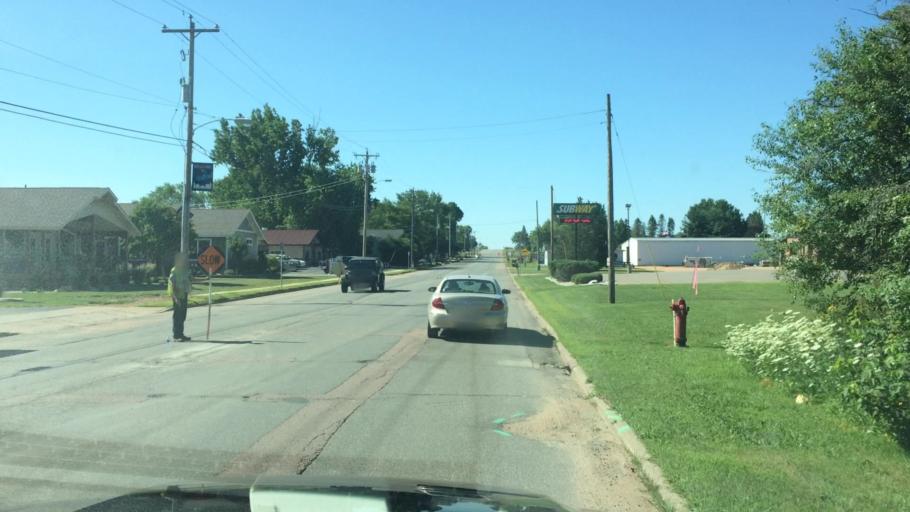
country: US
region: Wisconsin
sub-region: Marathon County
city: Stratford
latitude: 44.7975
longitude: -90.0792
